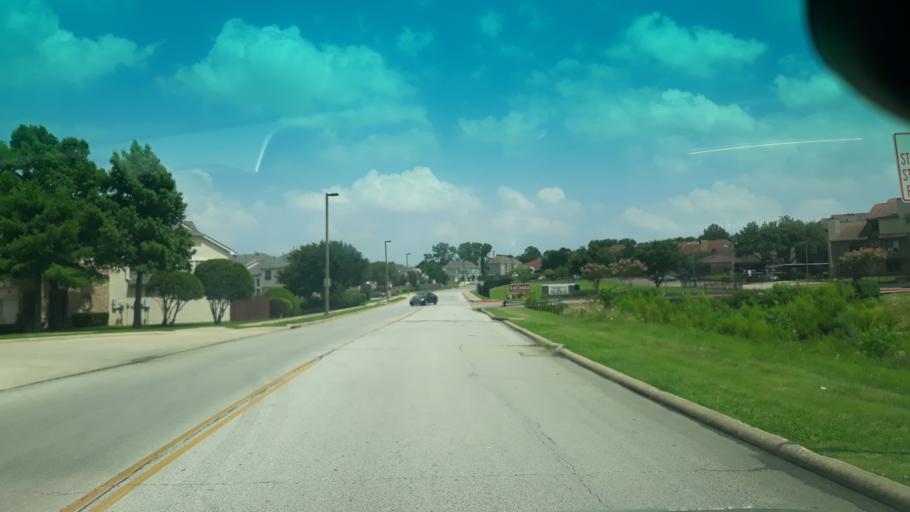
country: US
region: Texas
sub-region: Dallas County
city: Irving
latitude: 32.8650
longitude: -96.9824
